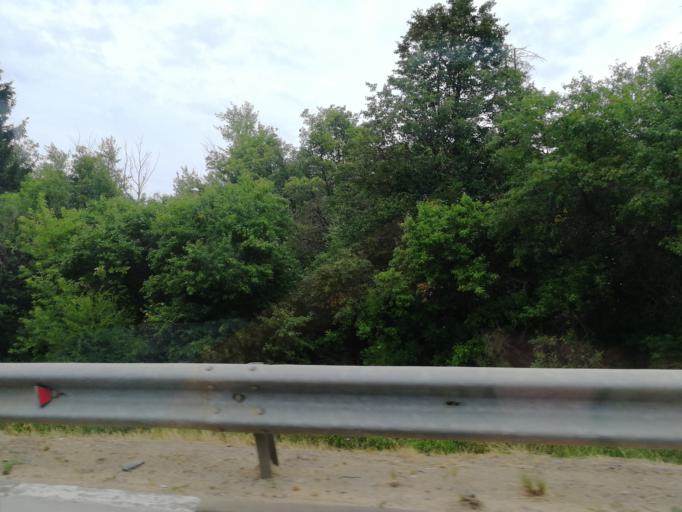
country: RU
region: Tula
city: Bogoroditsk
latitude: 53.7192
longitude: 38.1068
